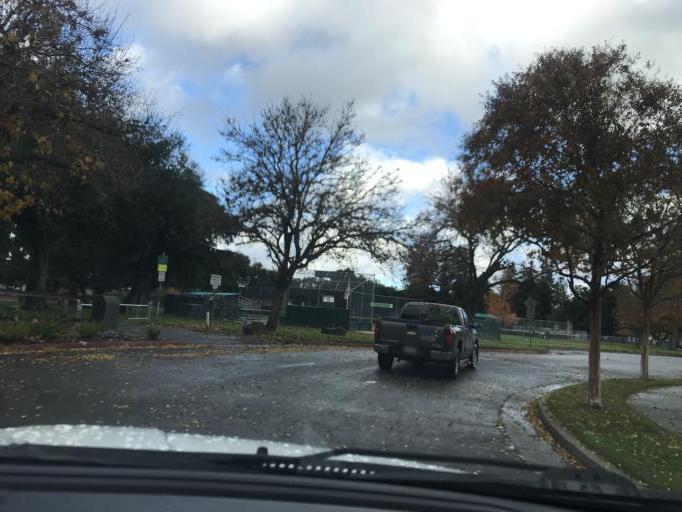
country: US
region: California
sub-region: Santa Clara County
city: Buena Vista
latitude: 37.3022
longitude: -121.9100
